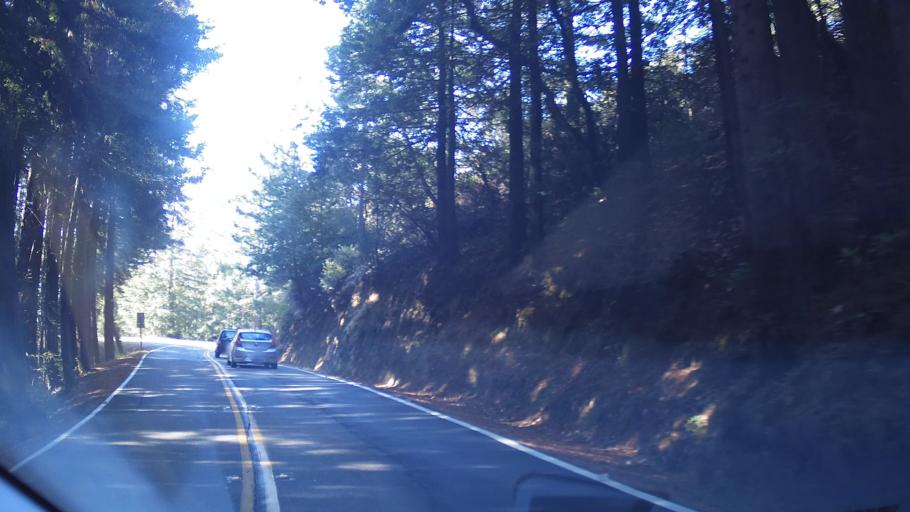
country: US
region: California
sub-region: Marin County
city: Mill Valley
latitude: 37.9107
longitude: -122.5880
